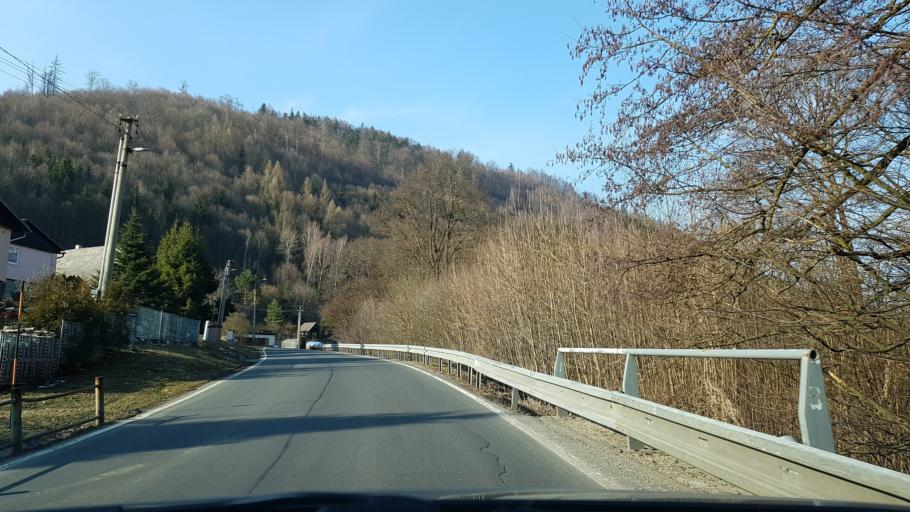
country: CZ
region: Olomoucky
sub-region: Okres Sumperk
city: Hanusovice
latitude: 50.0624
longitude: 16.9247
